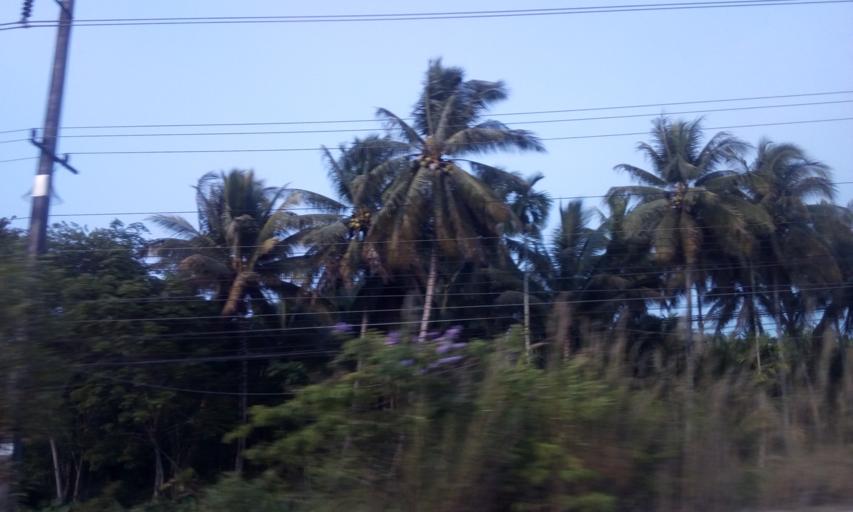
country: TH
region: Trat
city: Khao Saming
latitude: 12.3994
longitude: 102.3481
